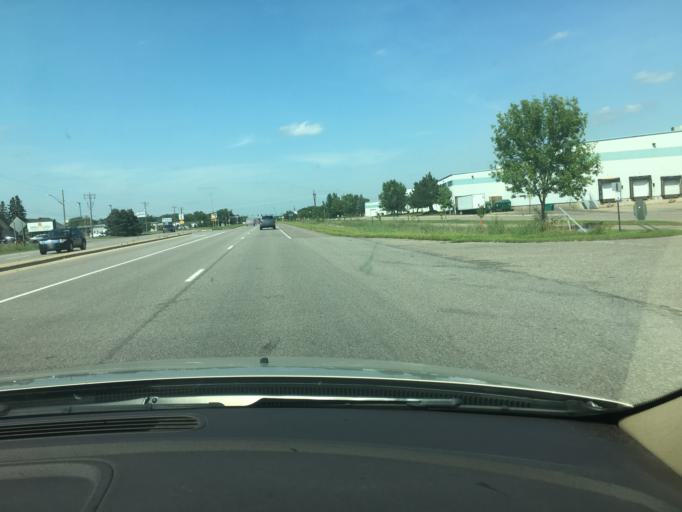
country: US
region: Minnesota
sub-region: Stearns County
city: Saint Augusta
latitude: 45.5180
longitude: -94.1605
